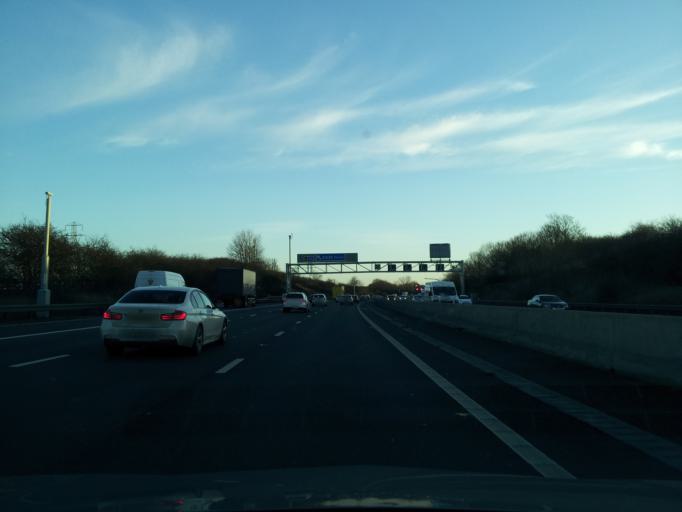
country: GB
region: England
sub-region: Central Bedfordshire
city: Steppingley
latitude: 51.9804
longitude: -0.5266
